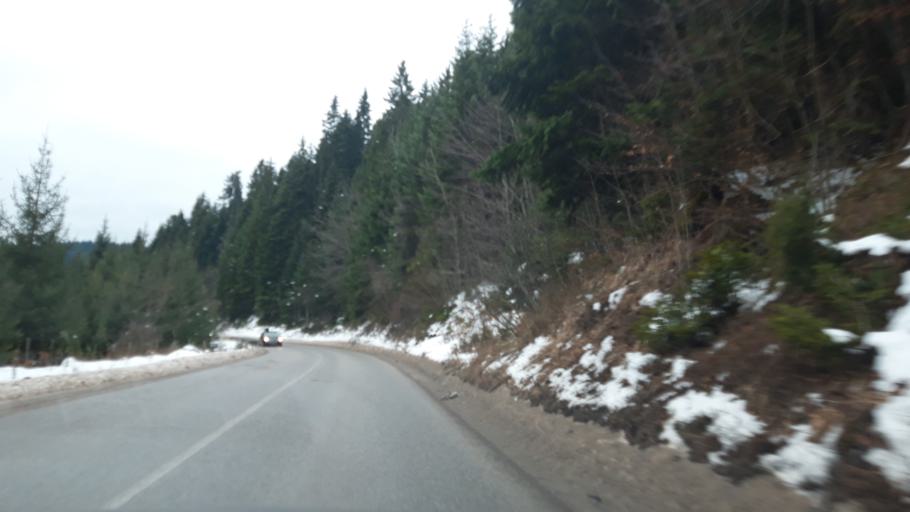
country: BA
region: Republika Srpska
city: Koran
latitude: 43.7962
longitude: 18.5553
